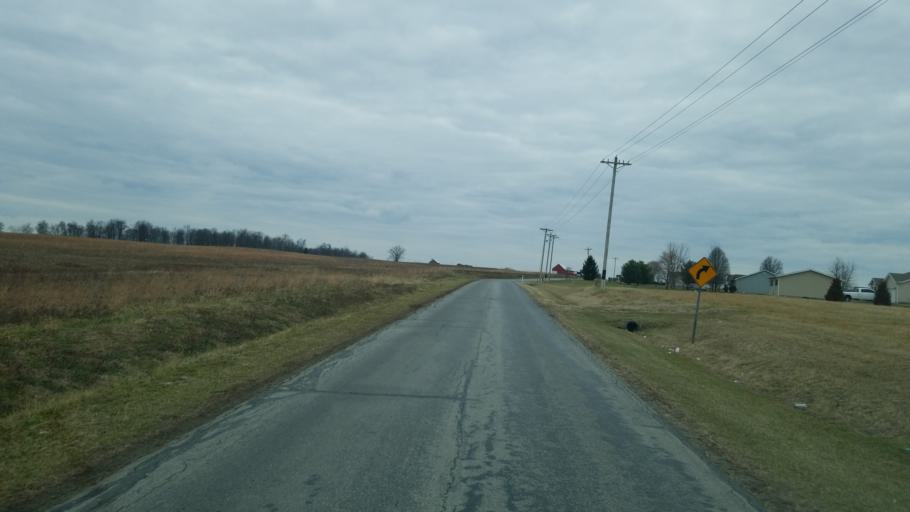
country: US
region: Ohio
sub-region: Highland County
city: Hillsboro
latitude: 39.2277
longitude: -83.4865
